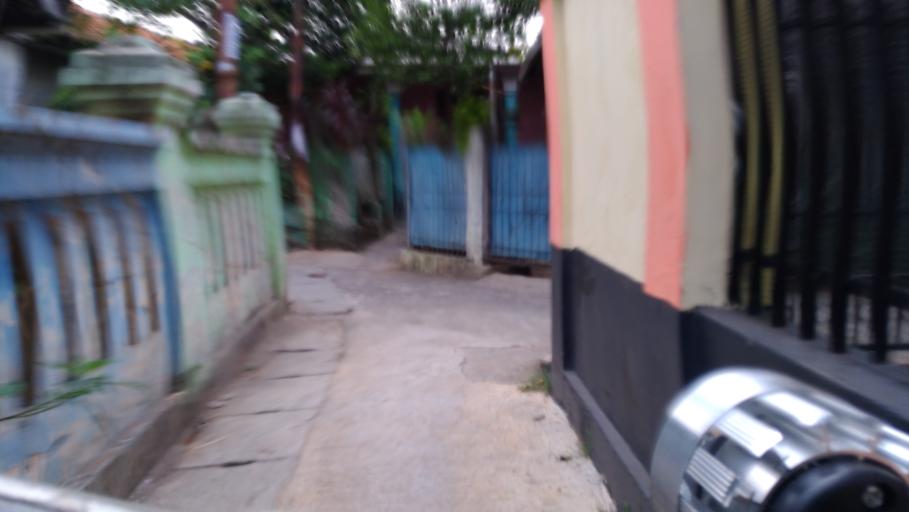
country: ID
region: West Java
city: Depok
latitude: -6.3556
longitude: 106.8707
